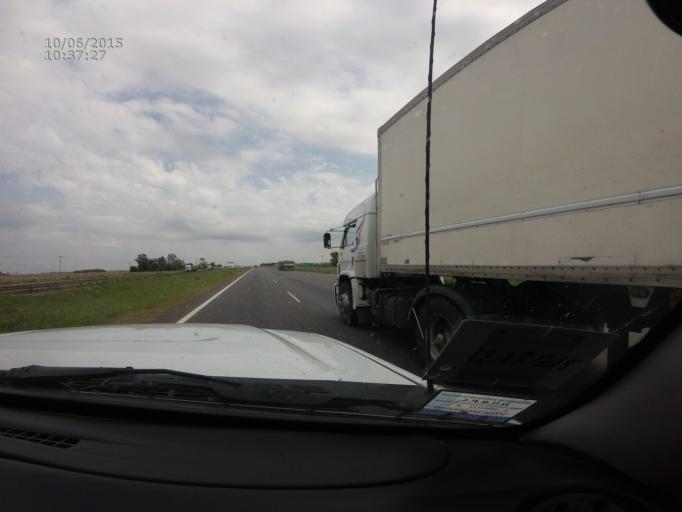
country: AR
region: Buenos Aires
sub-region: Partido de Ramallo
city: Ramallo
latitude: -33.5457
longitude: -60.0943
